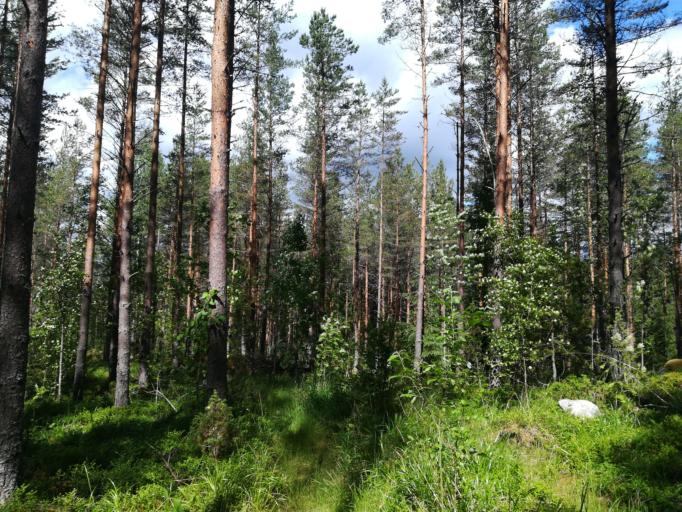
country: FI
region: Southern Savonia
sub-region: Mikkeli
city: Hirvensalmi
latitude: 61.6267
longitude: 26.7650
